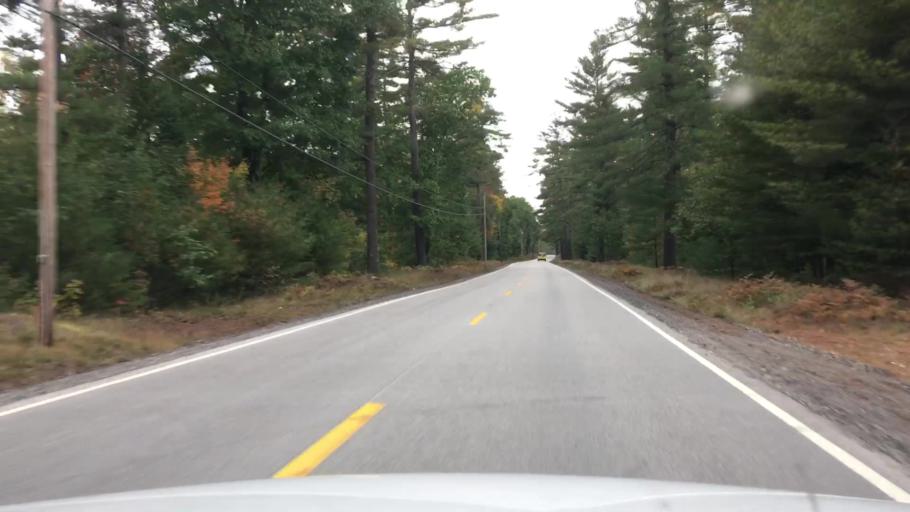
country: US
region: Maine
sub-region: Cumberland County
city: Harrison
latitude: 44.2203
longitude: -70.6914
